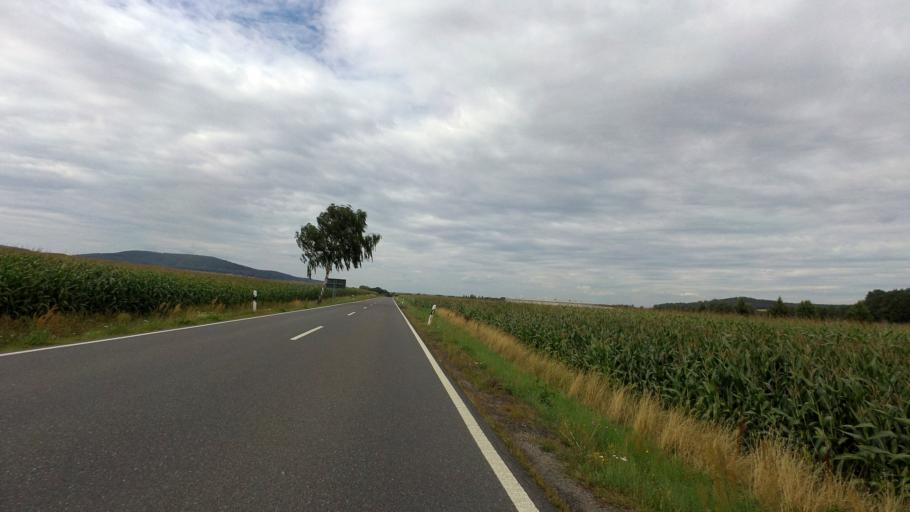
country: DE
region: Saxony
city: Rammenau
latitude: 51.1856
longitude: 14.1381
